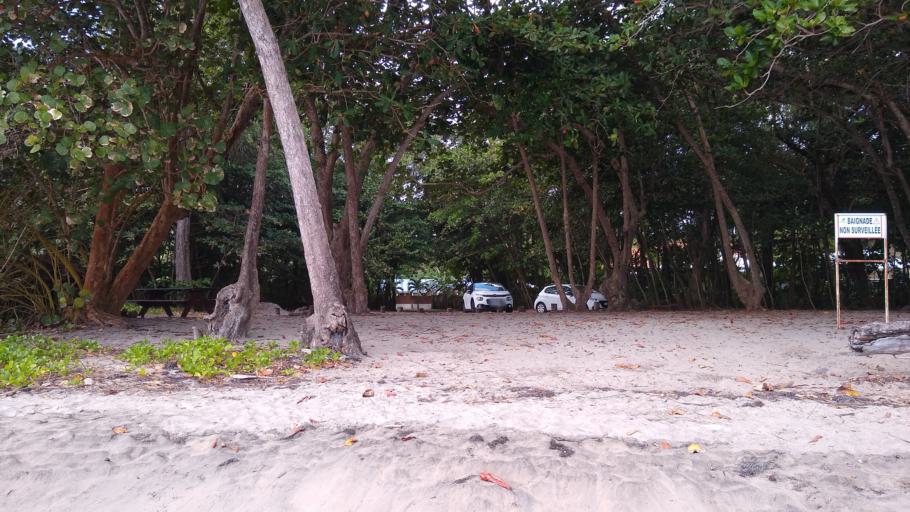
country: MQ
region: Martinique
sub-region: Martinique
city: Les Trois-Ilets
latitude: 14.4748
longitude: -61.0381
